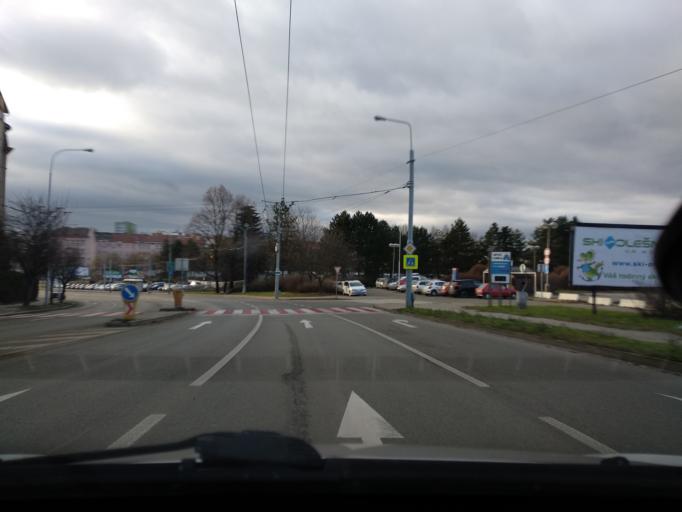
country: CZ
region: South Moravian
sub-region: Mesto Brno
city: Brno
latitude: 49.2106
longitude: 16.6112
